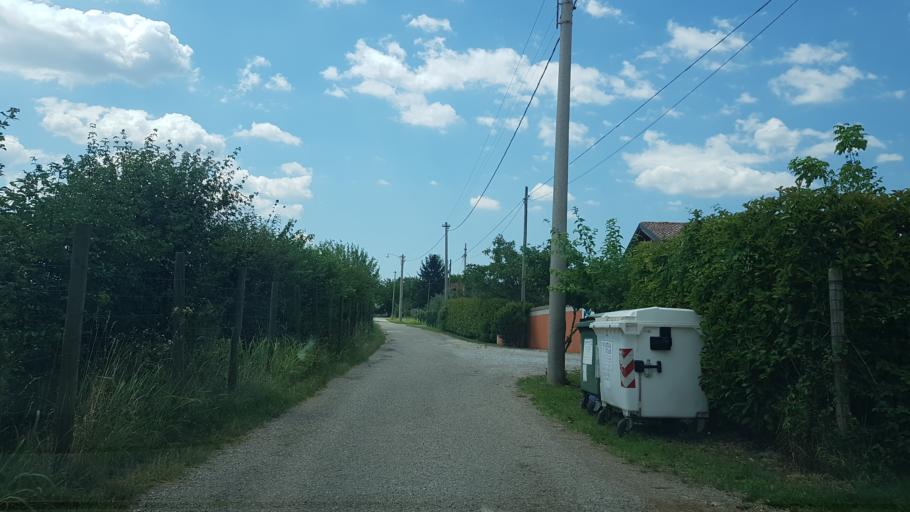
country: SI
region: Nova Gorica
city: Solkan
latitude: 45.9656
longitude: 13.6303
